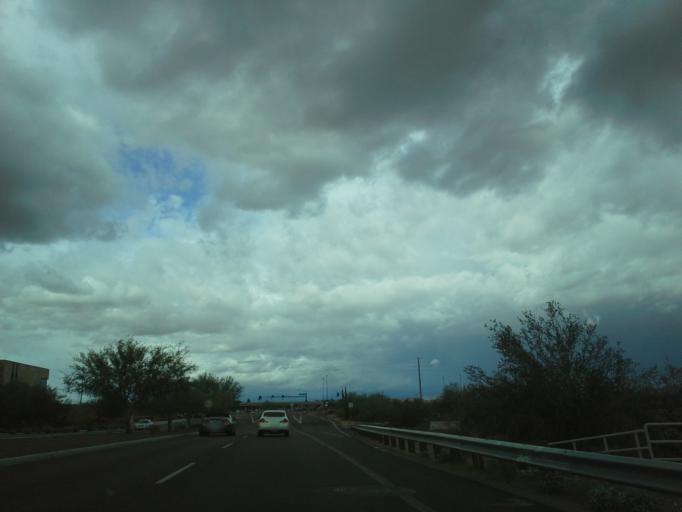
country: US
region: Arizona
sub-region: Maricopa County
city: Paradise Valley
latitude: 33.6668
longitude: -111.9773
